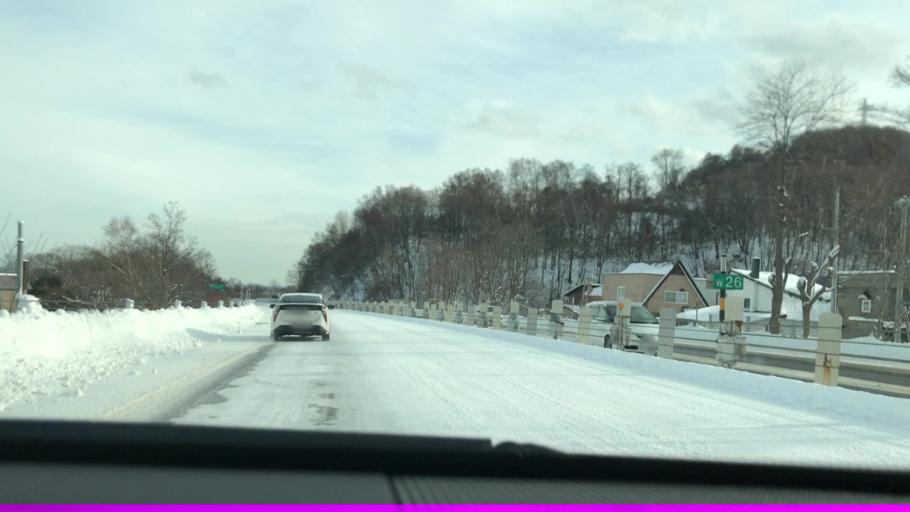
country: JP
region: Hokkaido
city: Otaru
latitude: 43.1413
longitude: 141.1465
